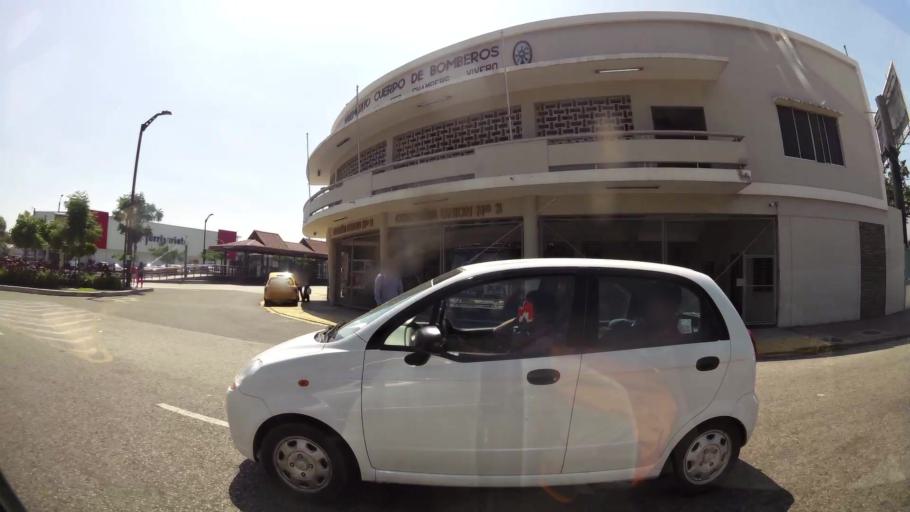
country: EC
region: Guayas
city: Guayaquil
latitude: -2.1818
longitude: -79.8918
